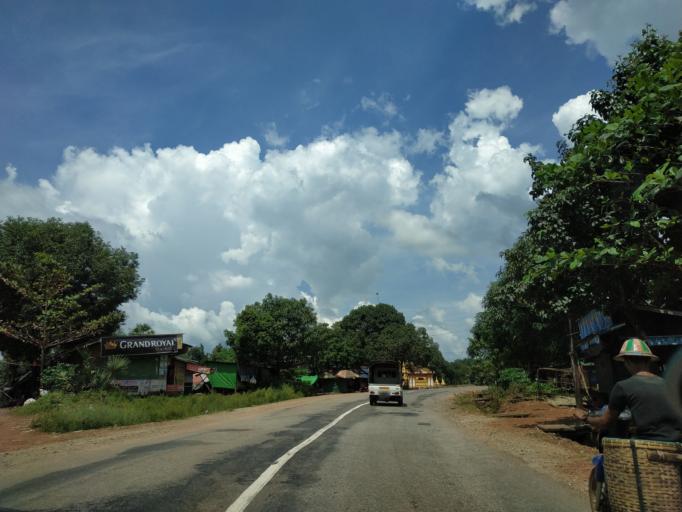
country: TH
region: Kanchanaburi
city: Sangkhla Buri
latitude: 15.3398
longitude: 97.8702
